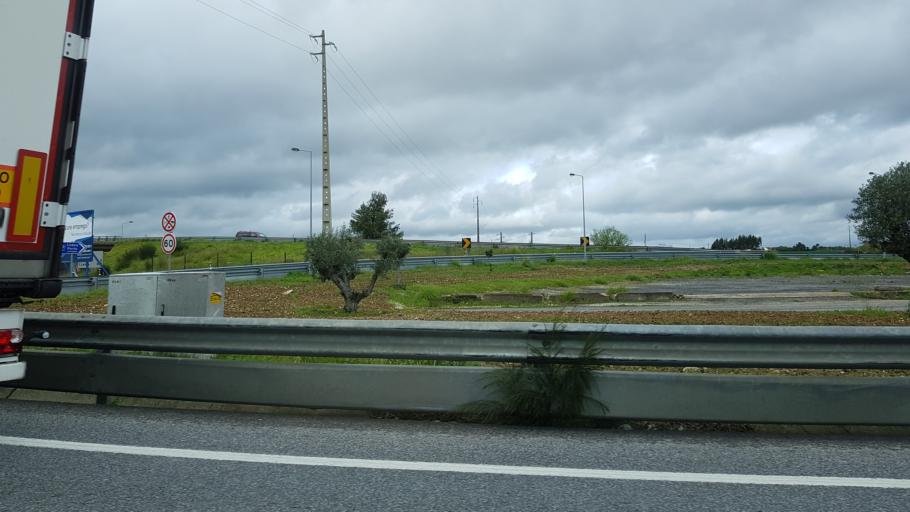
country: PT
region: Lisbon
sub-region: Alenquer
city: Carregado
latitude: 39.0333
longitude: -8.9805
